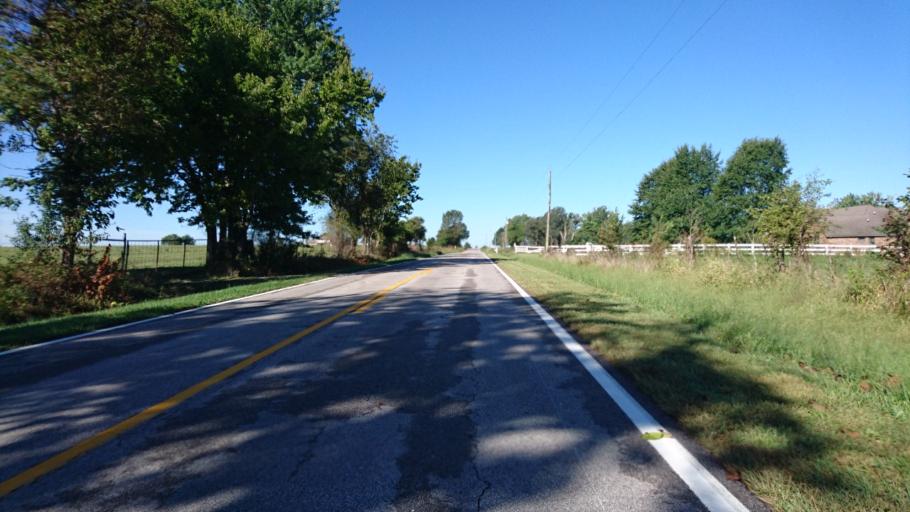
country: US
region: Missouri
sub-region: Greene County
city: Ash Grove
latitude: 37.1938
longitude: -93.6525
